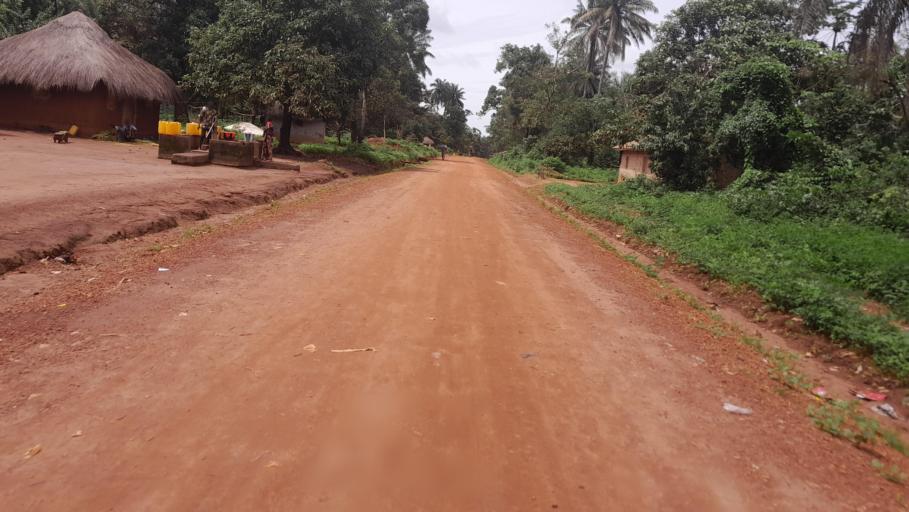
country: GN
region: Boke
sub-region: Boffa
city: Boffa
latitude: 10.0077
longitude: -13.8864
